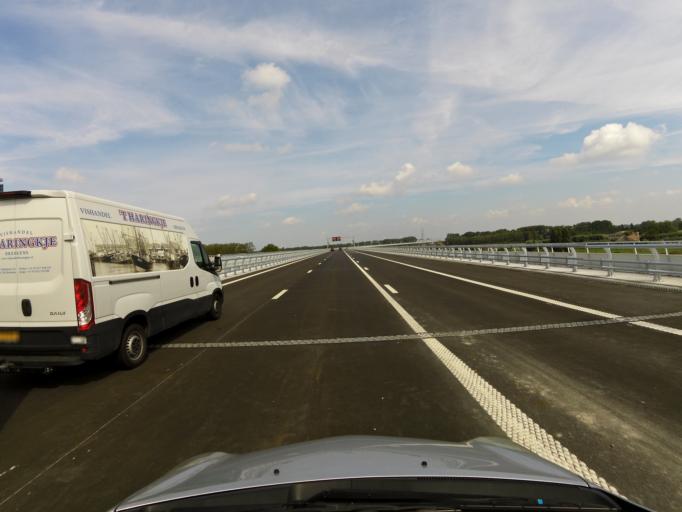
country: BE
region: Flanders
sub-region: Provincie West-Vlaanderen
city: Zuienkerke
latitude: 51.2672
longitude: 3.2006
